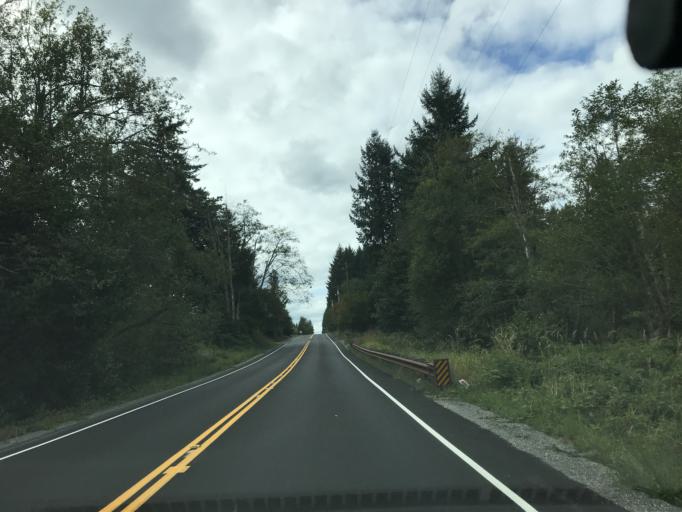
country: US
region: Washington
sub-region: King County
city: Black Diamond
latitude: 47.2868
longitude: -122.0031
